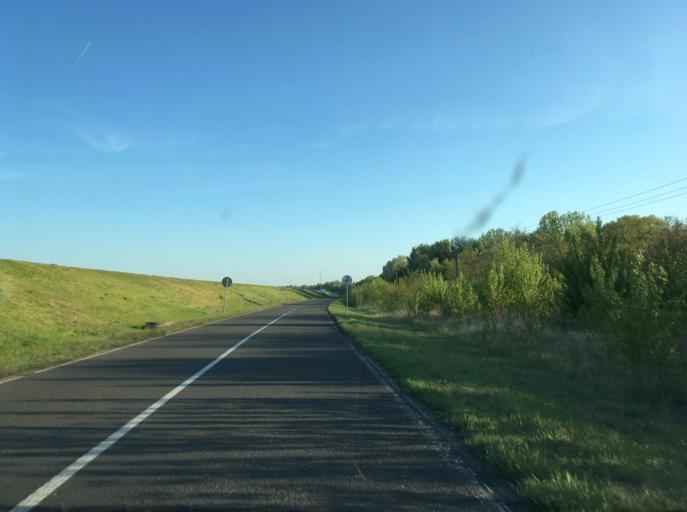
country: HU
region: Gyor-Moson-Sopron
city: Rajka
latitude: 48.0151
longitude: 17.2518
